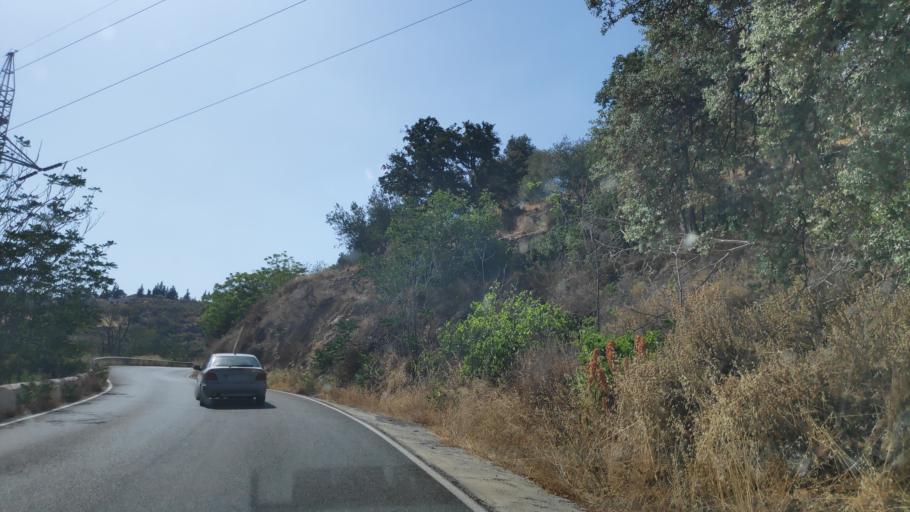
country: ES
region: Andalusia
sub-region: Provincia de Granada
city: Soportujar
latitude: 36.9228
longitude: -3.3826
